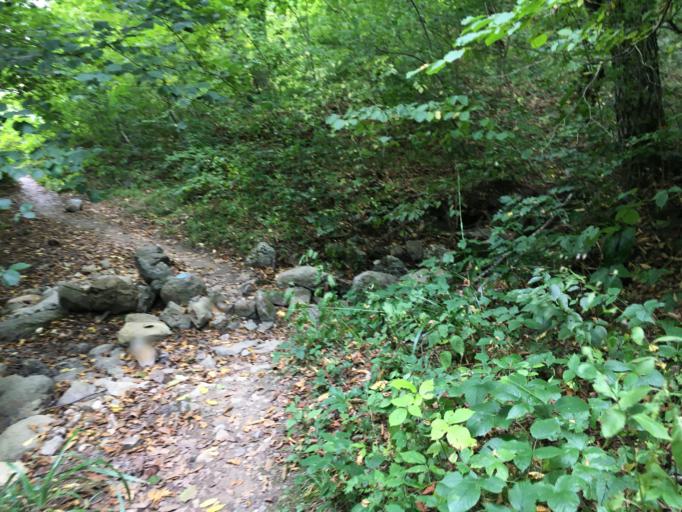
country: RU
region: Krasnodarskiy
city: Tuapse
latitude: 44.2585
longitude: 39.2177
